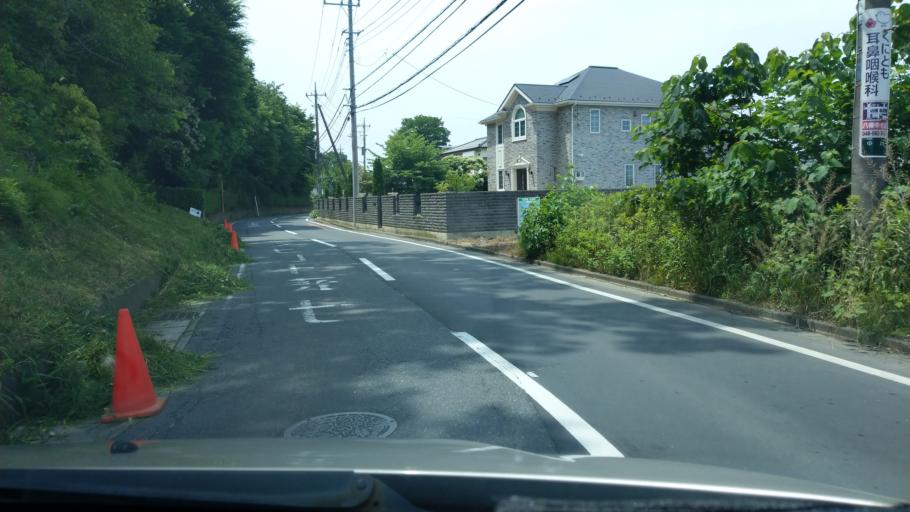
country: JP
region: Saitama
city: Saitama
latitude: 35.9079
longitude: 139.6505
